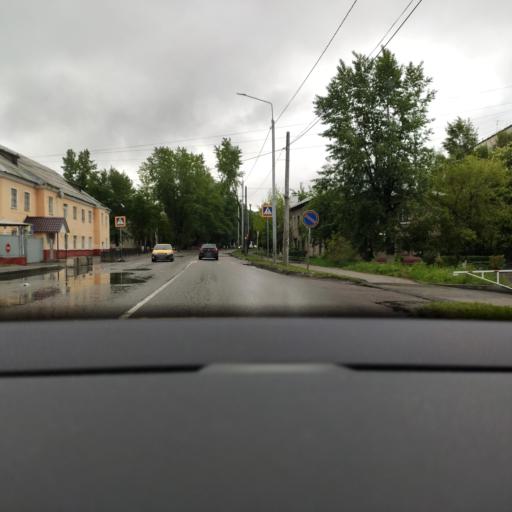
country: RU
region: Moskovskaya
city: Saltykovka
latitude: 55.7477
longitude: 37.9726
